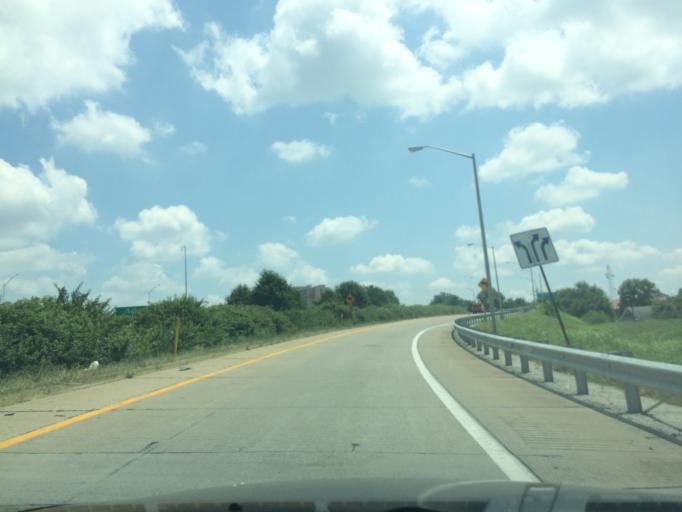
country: US
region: Kentucky
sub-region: Jefferson County
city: West Buechel
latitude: 38.2013
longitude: -85.6906
